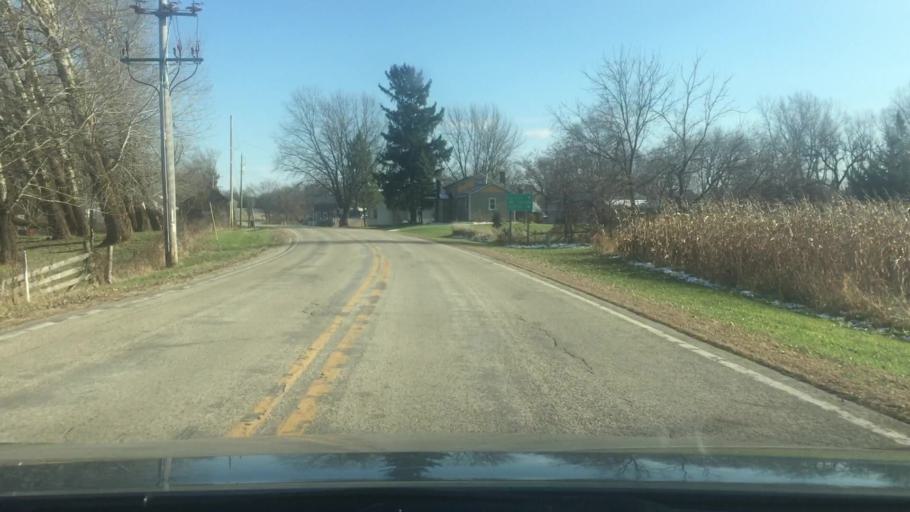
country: US
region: Wisconsin
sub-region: Jefferson County
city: Palmyra
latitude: 42.9371
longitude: -88.5883
